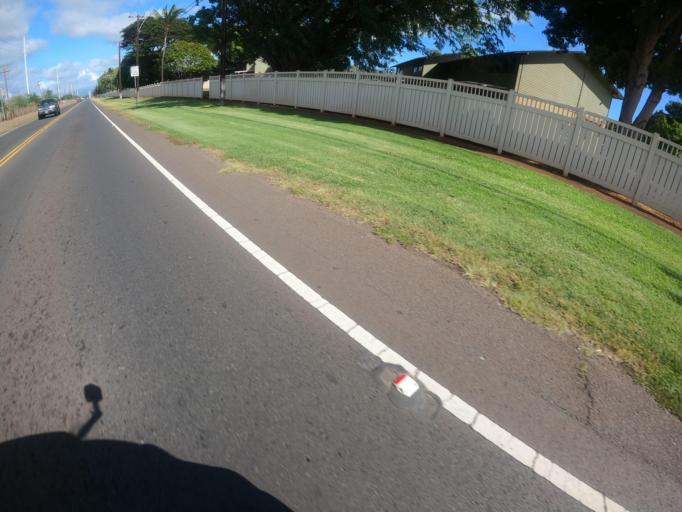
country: US
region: Hawaii
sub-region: Honolulu County
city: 'Ewa Villages
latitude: 21.3274
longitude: -158.0600
